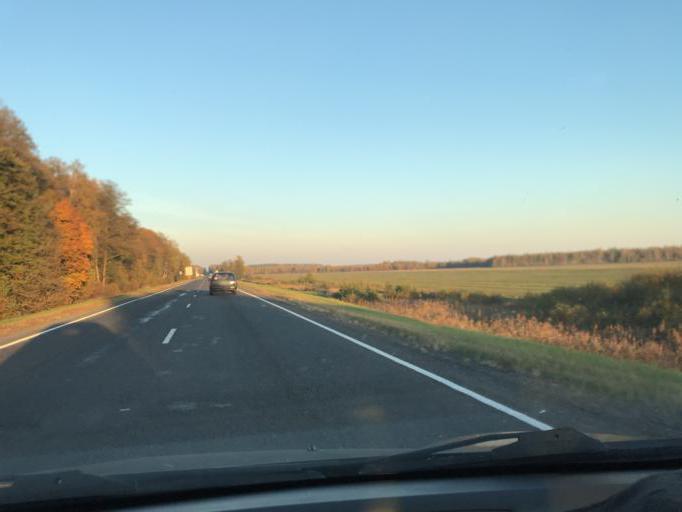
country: BY
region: Mogilev
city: Hlusk
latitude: 53.0634
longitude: 28.5173
